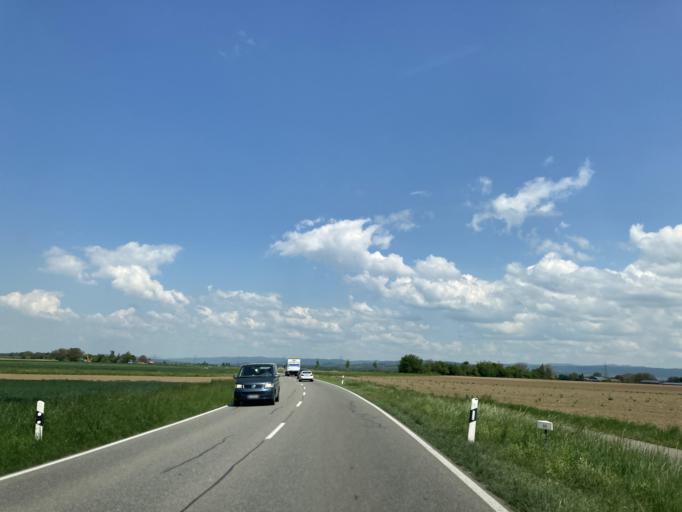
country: DE
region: Baden-Wuerttemberg
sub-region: Freiburg Region
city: Endingen
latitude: 48.1523
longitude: 7.7085
